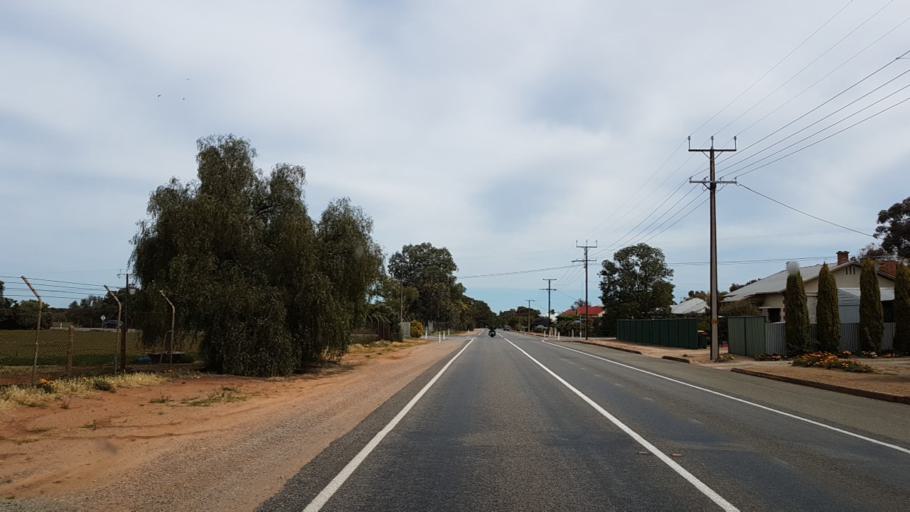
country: AU
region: South Australia
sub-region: Port Pirie City and Dists
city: Crystal Brook
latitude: -33.2610
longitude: 138.3550
